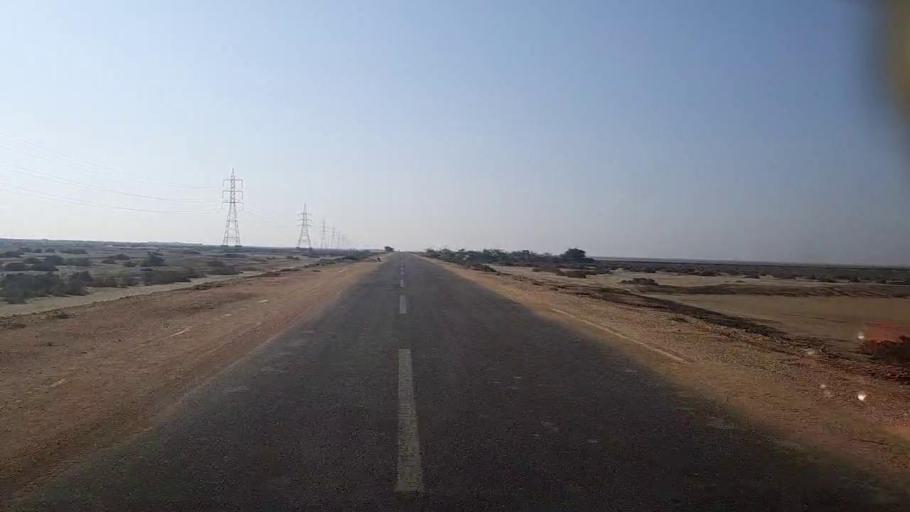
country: PK
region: Sindh
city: Mirpur Sakro
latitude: 24.6185
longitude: 67.4970
